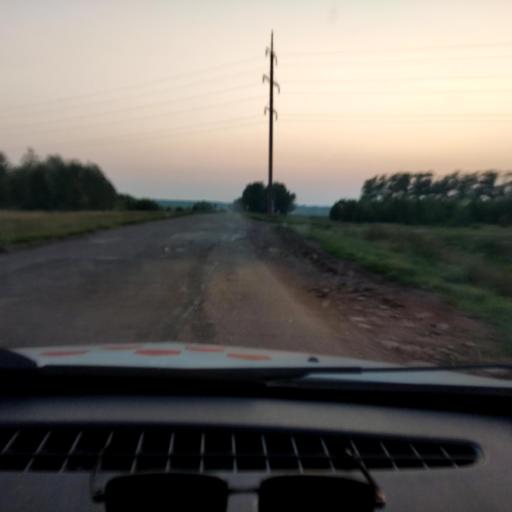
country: RU
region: Bashkortostan
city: Ulukulevo
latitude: 54.3698
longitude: 56.4255
